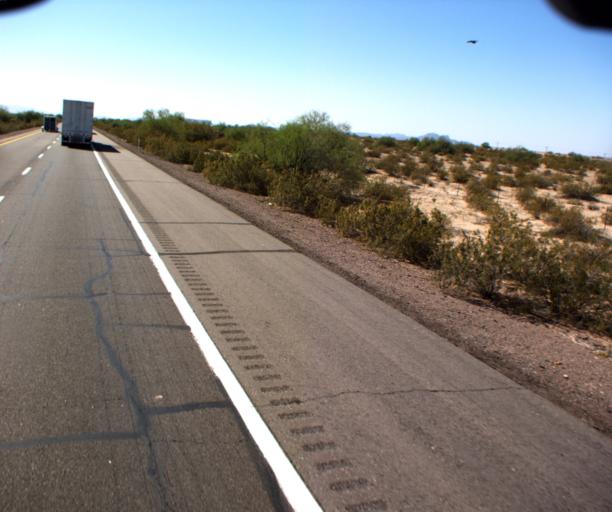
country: US
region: Arizona
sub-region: Yuma County
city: Wellton
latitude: 32.7070
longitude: -113.8661
